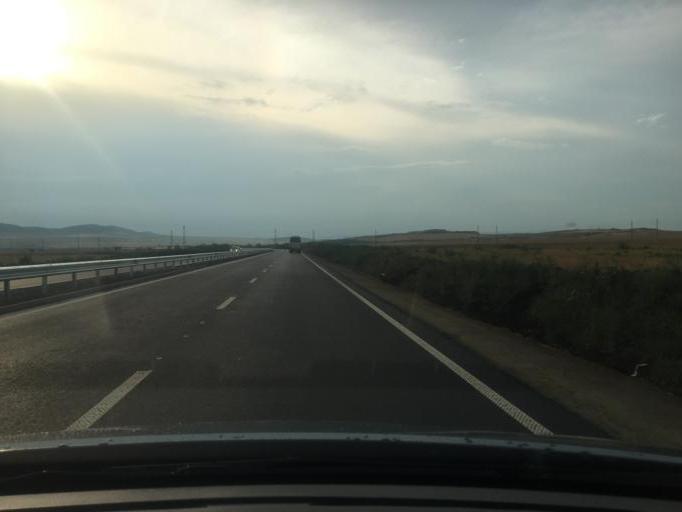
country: BG
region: Burgas
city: Aheloy
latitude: 42.6536
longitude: 27.6622
